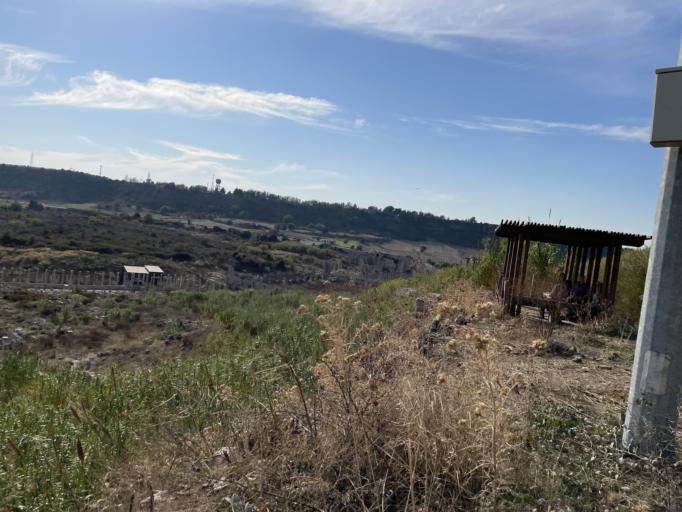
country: TR
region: Antalya
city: Aksu
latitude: 36.9668
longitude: 30.8556
